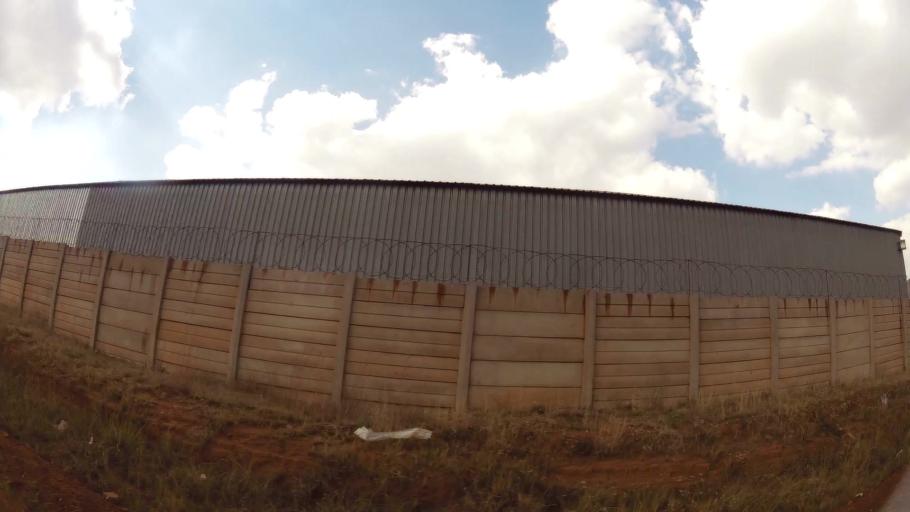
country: ZA
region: Mpumalanga
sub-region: Nkangala District Municipality
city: Delmas
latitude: -26.1340
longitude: 28.6787
